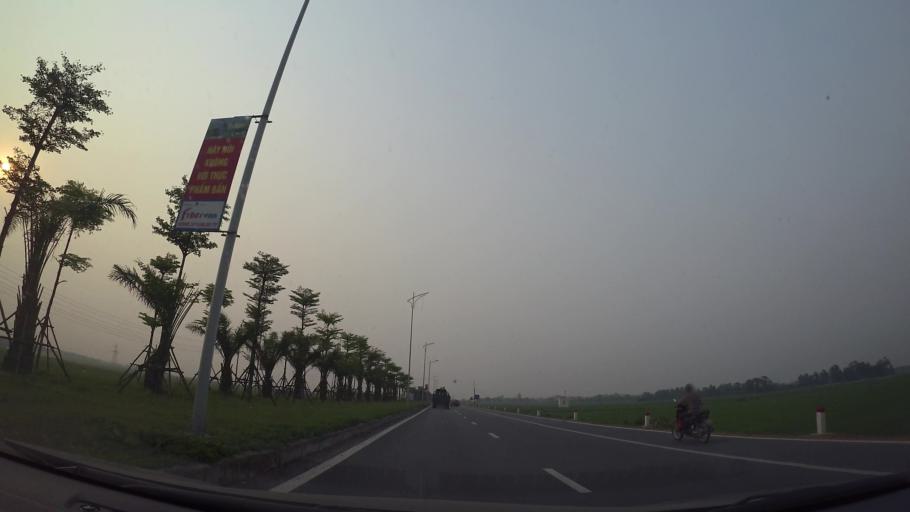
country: VN
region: Ha Noi
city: Kim Bai
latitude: 20.8852
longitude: 105.7975
